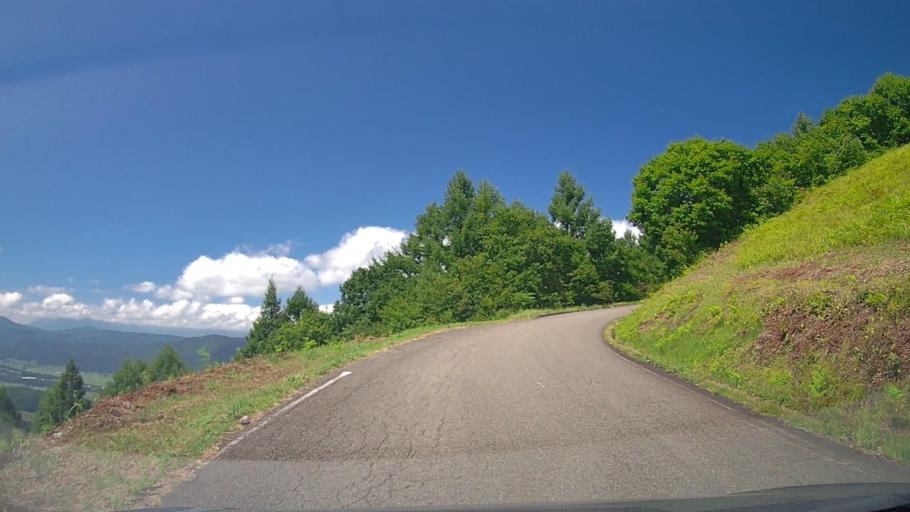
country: JP
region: Nagano
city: Iiyama
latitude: 36.9324
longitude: 138.4578
